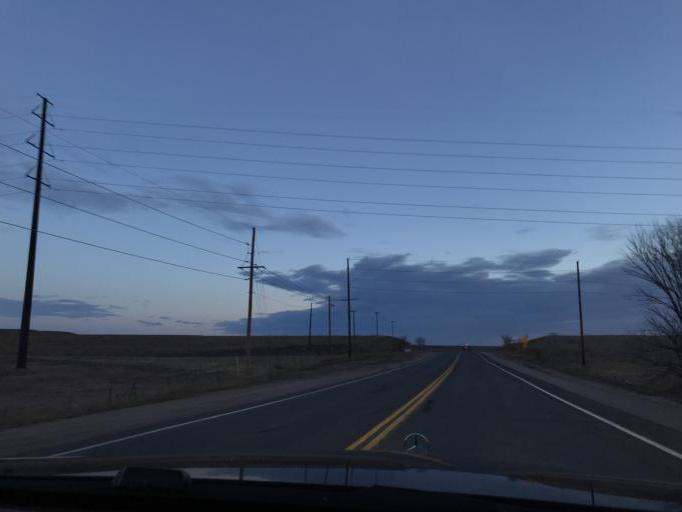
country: US
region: Colorado
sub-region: Boulder County
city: Superior
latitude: 39.8890
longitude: -105.1656
